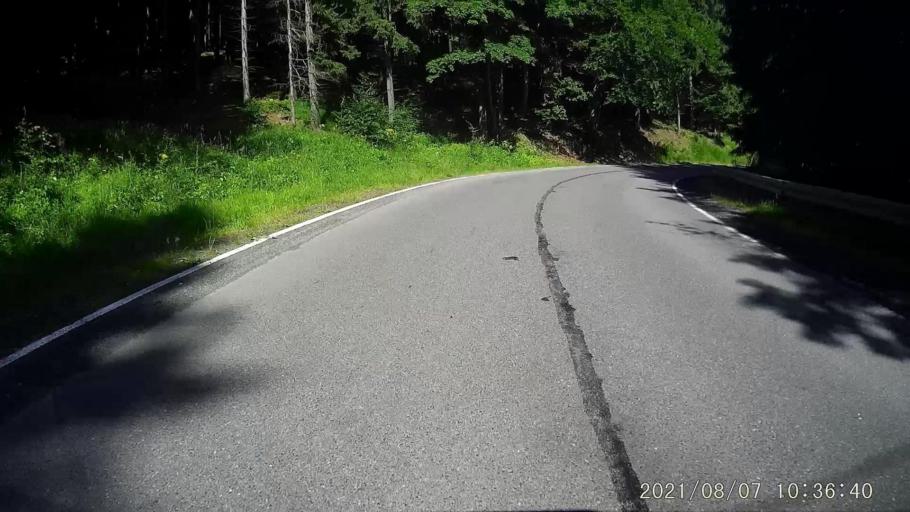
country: PL
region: Lower Silesian Voivodeship
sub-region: Powiat klodzki
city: Duszniki-Zdroj
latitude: 50.3611
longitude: 16.3719
